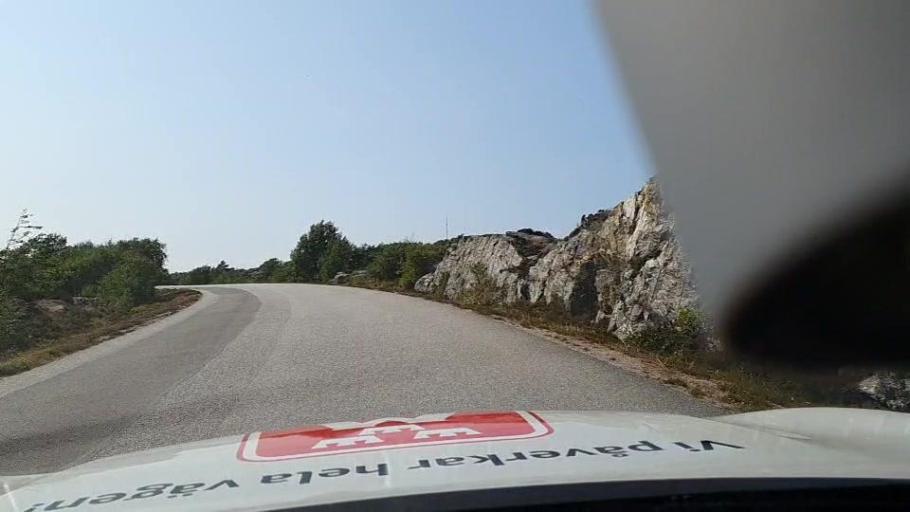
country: SE
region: Vaestra Goetaland
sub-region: Lysekils Kommun
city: Lysekil
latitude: 58.1199
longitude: 11.4668
